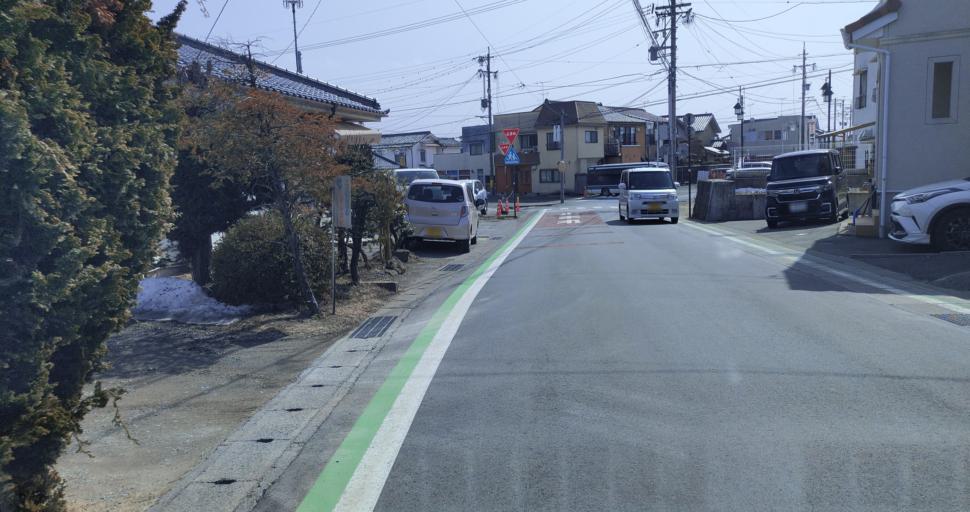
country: JP
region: Nagano
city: Saku
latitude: 36.2723
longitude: 138.4811
